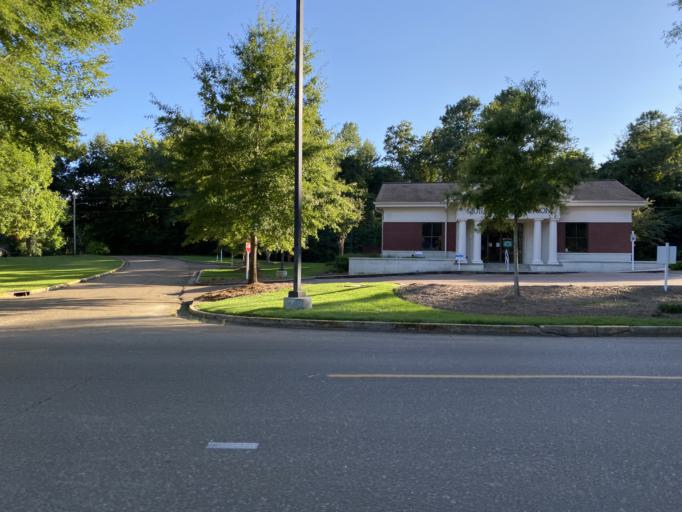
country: US
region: Mississippi
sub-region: Hinds County
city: Raymond
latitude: 32.2543
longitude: -90.4174
